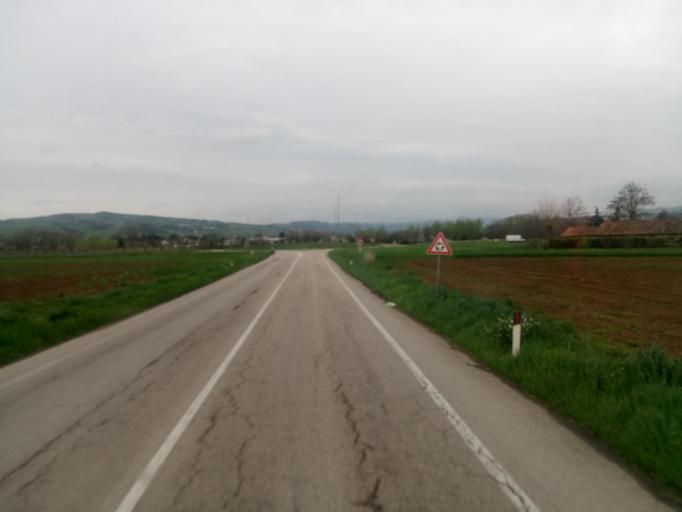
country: IT
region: Emilia-Romagna
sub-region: Forli-Cesena
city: Meldola
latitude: 44.1487
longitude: 12.0719
